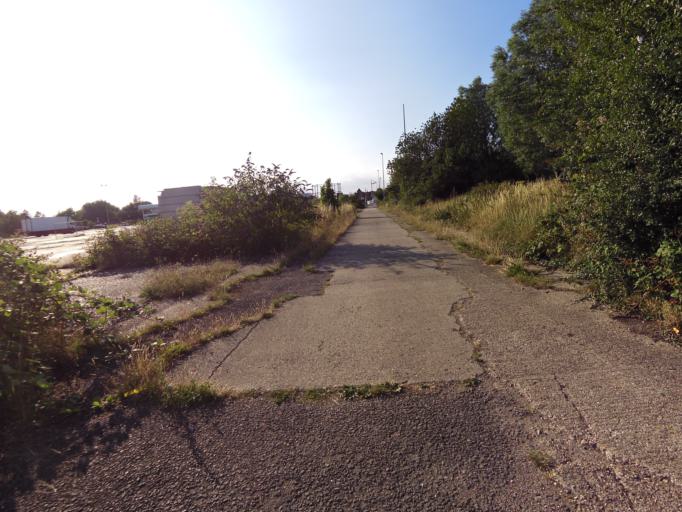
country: GB
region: England
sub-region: Essex
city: Chelmsford
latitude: 51.7297
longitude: 0.4837
